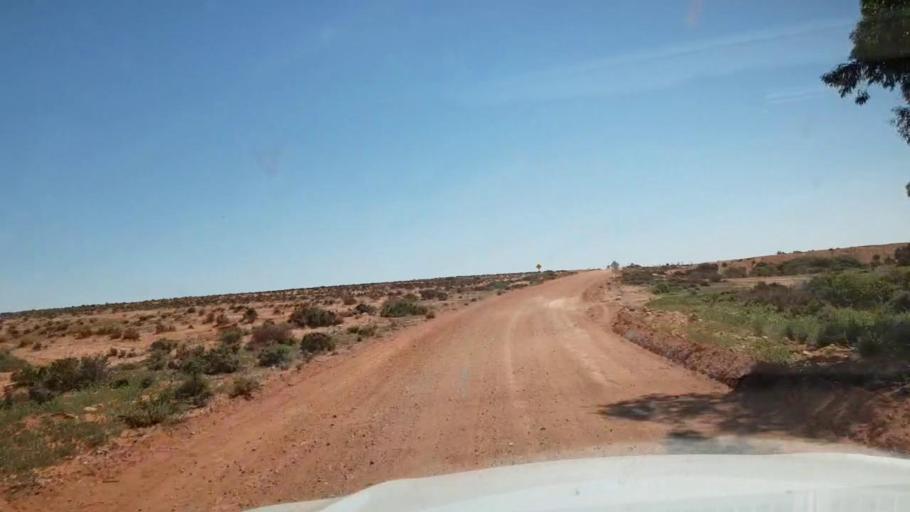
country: AU
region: South Australia
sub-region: Whyalla
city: Whyalla
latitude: -32.6826
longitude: 137.0890
